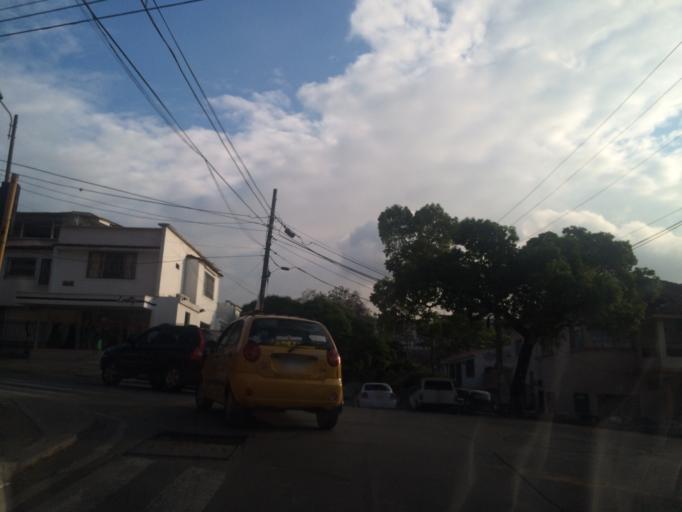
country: CO
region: Valle del Cauca
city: Cali
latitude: 3.4370
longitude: -76.5452
